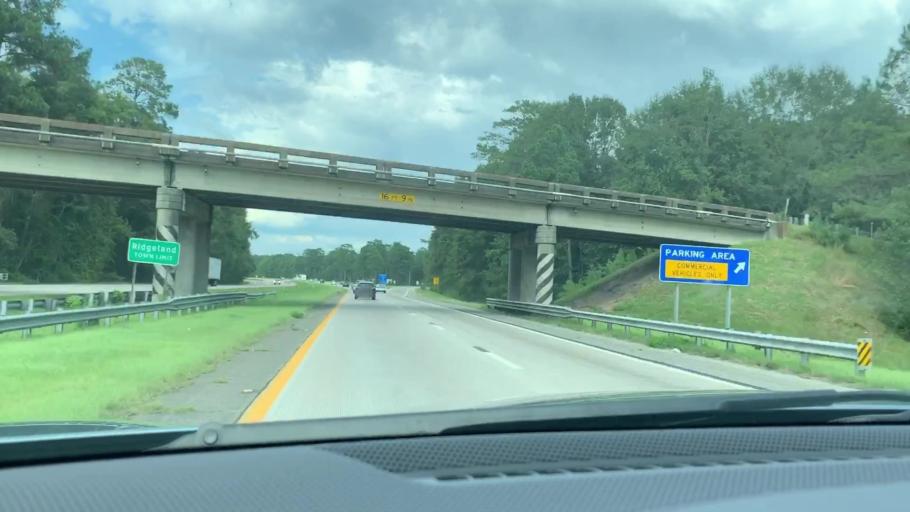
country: US
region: South Carolina
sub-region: Jasper County
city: Ridgeland
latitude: 32.4259
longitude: -81.0037
